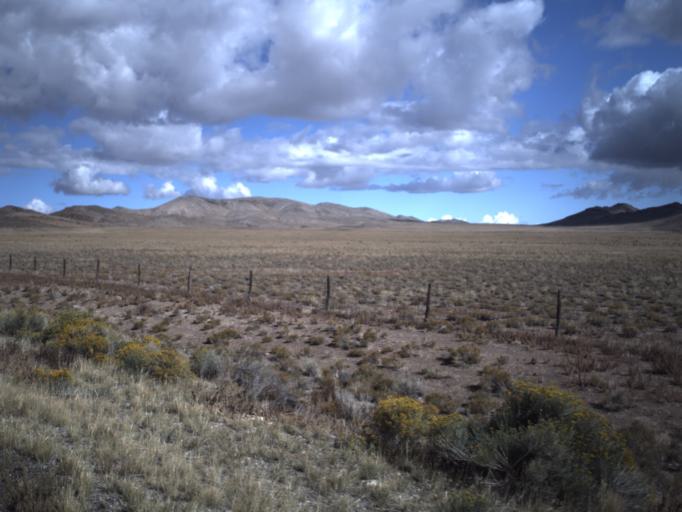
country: US
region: Utah
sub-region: Beaver County
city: Milford
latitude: 38.5957
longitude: -113.8254
